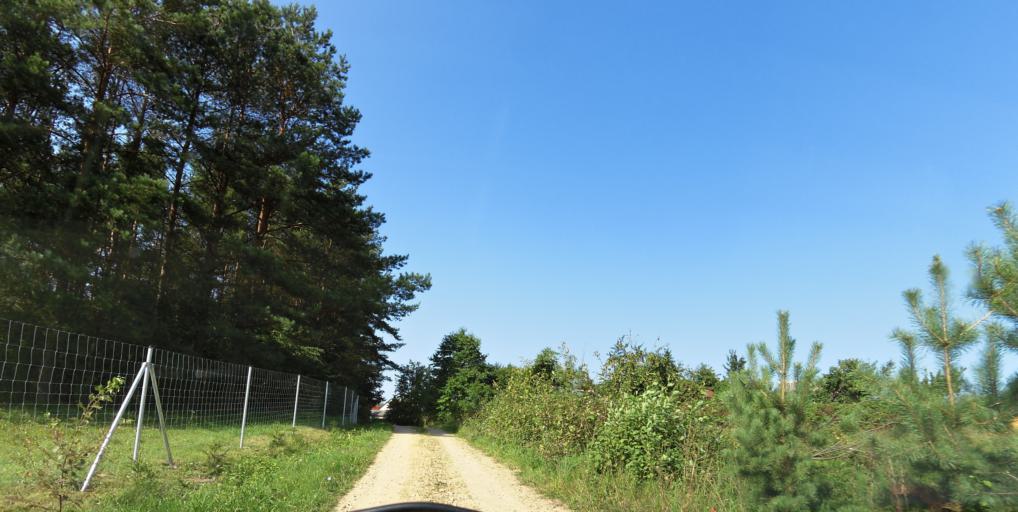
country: LT
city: Grigiskes
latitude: 54.7620
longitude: 25.0684
